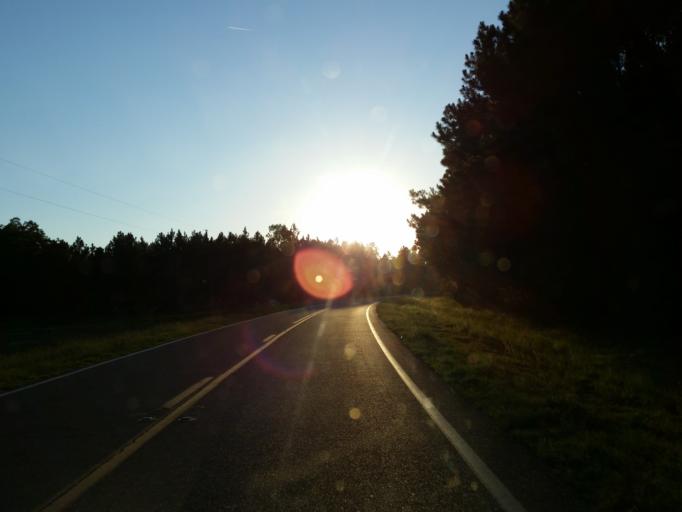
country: US
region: Georgia
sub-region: Berrien County
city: Nashville
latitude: 31.1798
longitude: -83.1364
